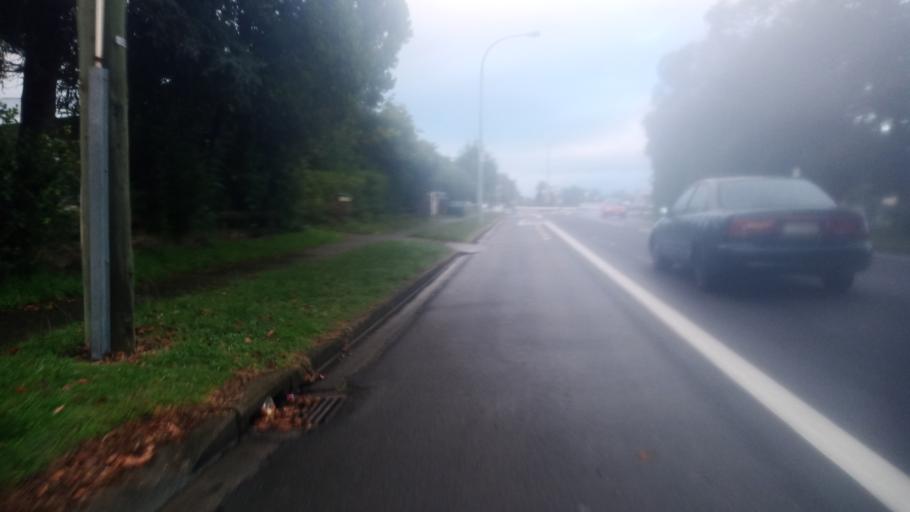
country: NZ
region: Gisborne
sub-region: Gisborne District
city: Gisborne
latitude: -38.6431
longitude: 178.0020
